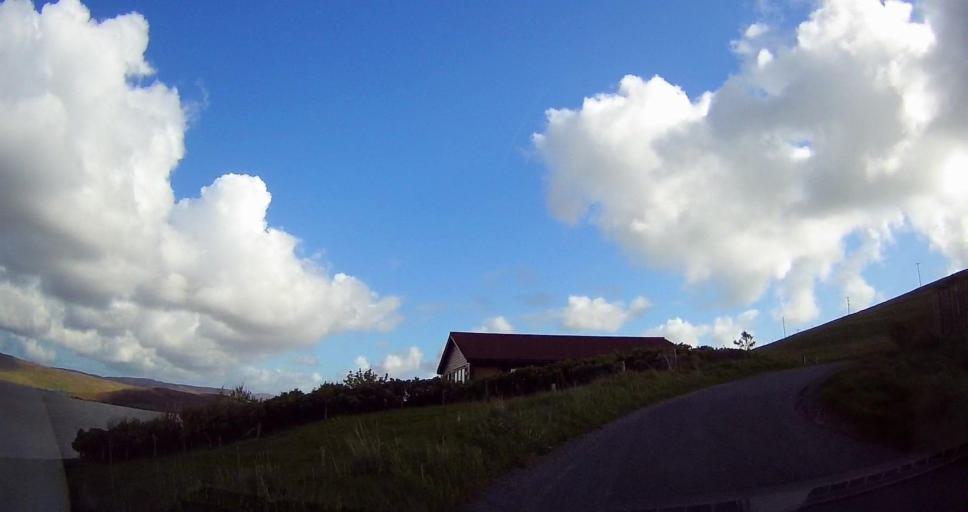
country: GB
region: Scotland
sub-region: Shetland Islands
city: Lerwick
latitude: 60.3725
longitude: -1.3820
